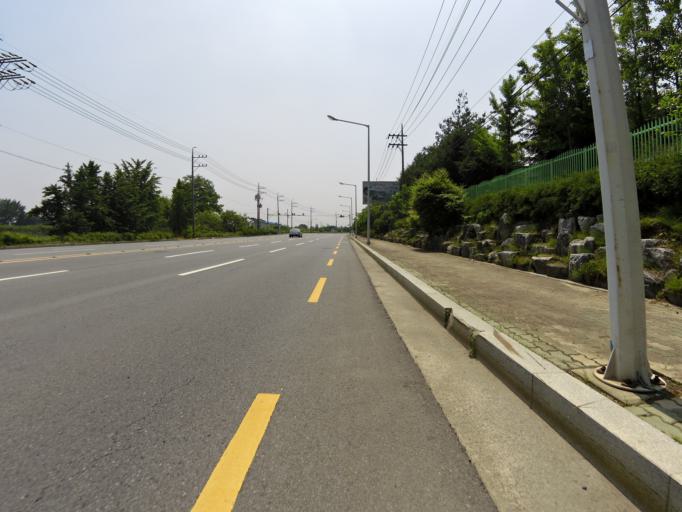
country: KR
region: Gyeongsangbuk-do
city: Gyeongsan-si
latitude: 35.8526
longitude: 128.7262
